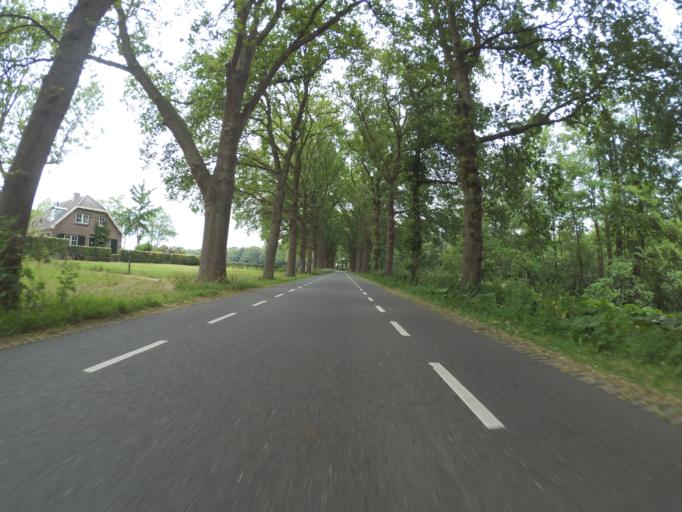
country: NL
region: Gelderland
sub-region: Gemeente Voorst
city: Voorst
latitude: 52.1465
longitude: 6.1415
